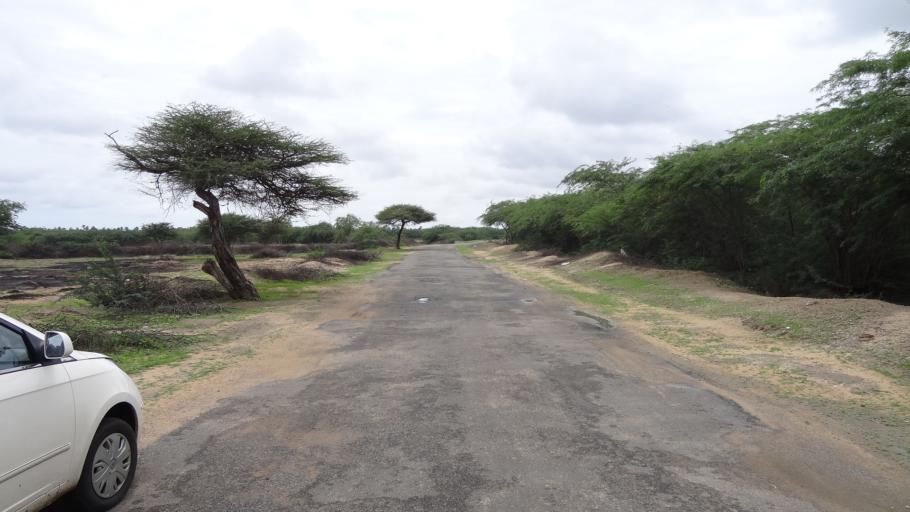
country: IN
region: Tamil Nadu
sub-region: Ramanathapuram
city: Sayalkudi
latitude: 9.1532
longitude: 78.3696
